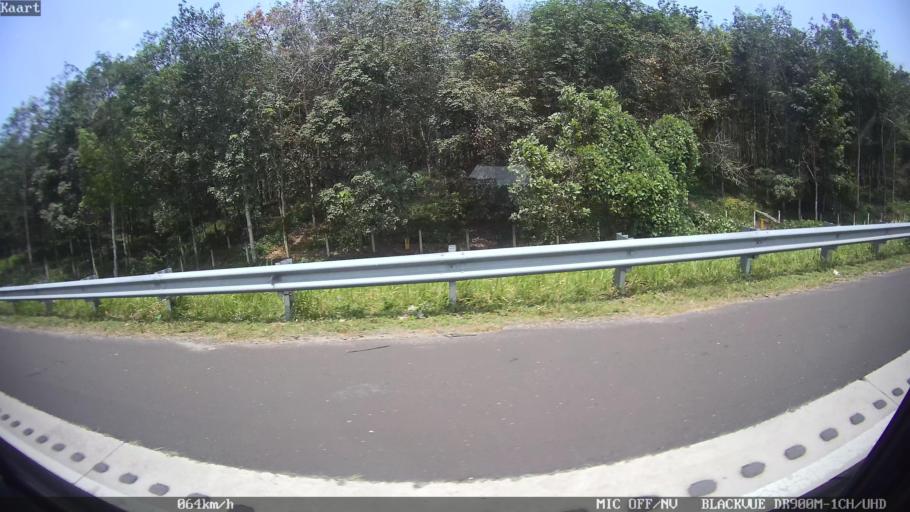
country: ID
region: Lampung
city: Kedaton
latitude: -5.3728
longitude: 105.3274
